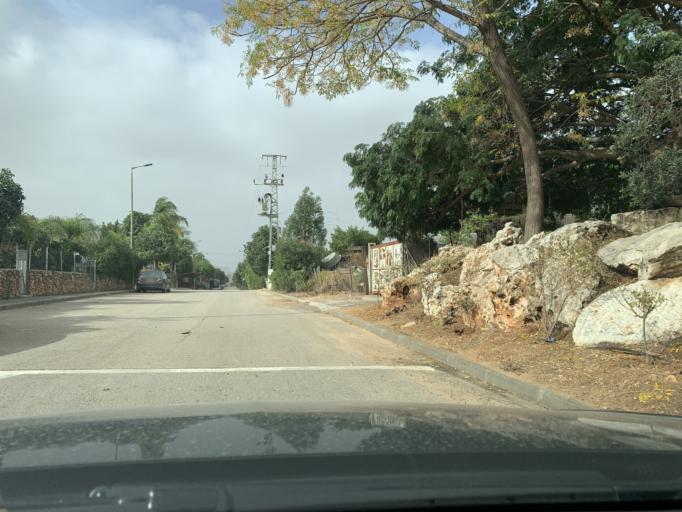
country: IL
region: Central District
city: Jaljulya
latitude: 32.1581
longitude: 34.9434
